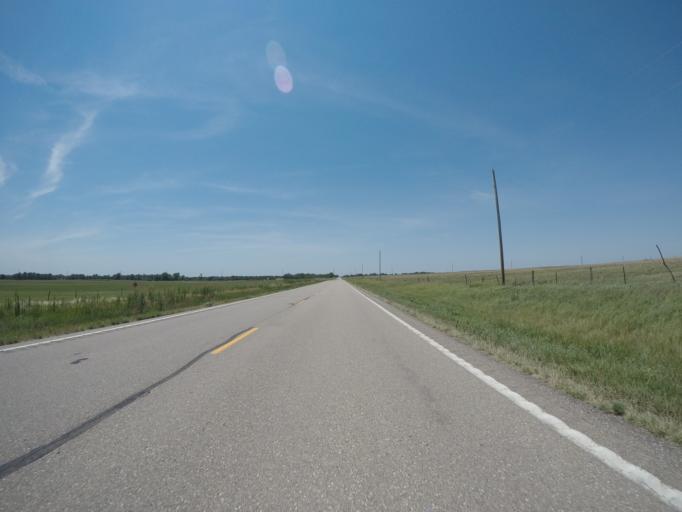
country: US
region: Kansas
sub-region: Dickinson County
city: Solomon
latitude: 39.0307
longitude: -97.5212
